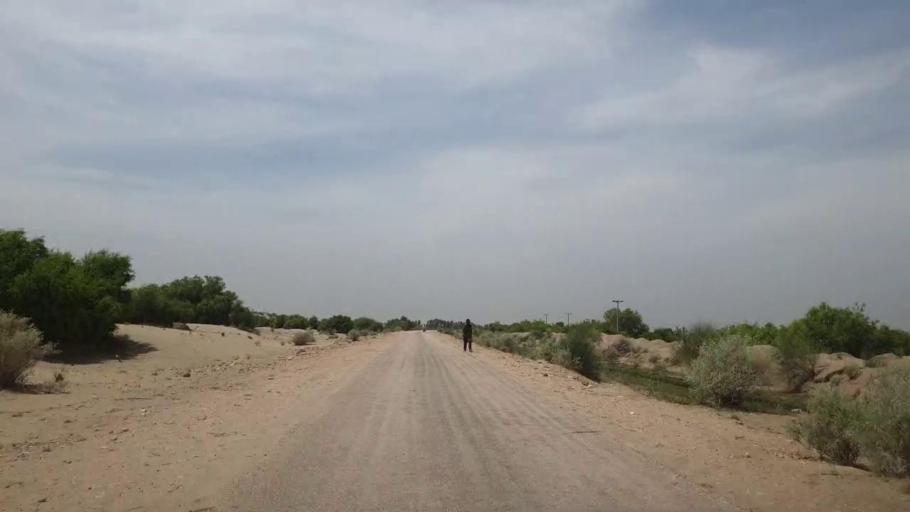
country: PK
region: Sindh
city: Kot Diji
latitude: 27.0986
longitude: 69.0795
